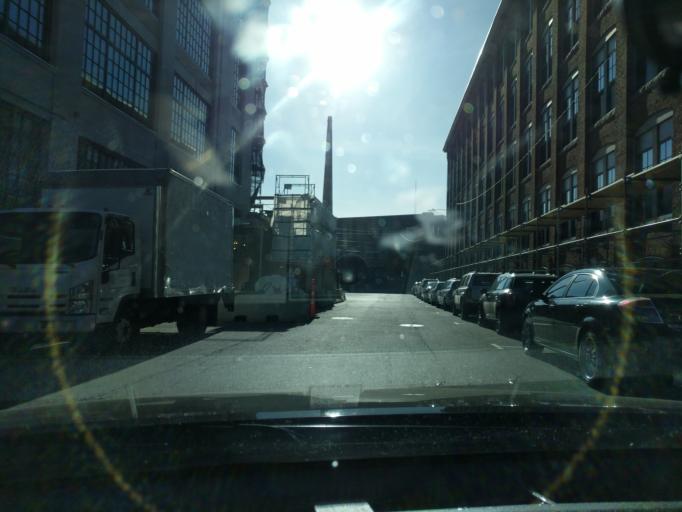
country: US
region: Massachusetts
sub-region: Middlesex County
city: Cambridge
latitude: 42.3607
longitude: -71.0980
